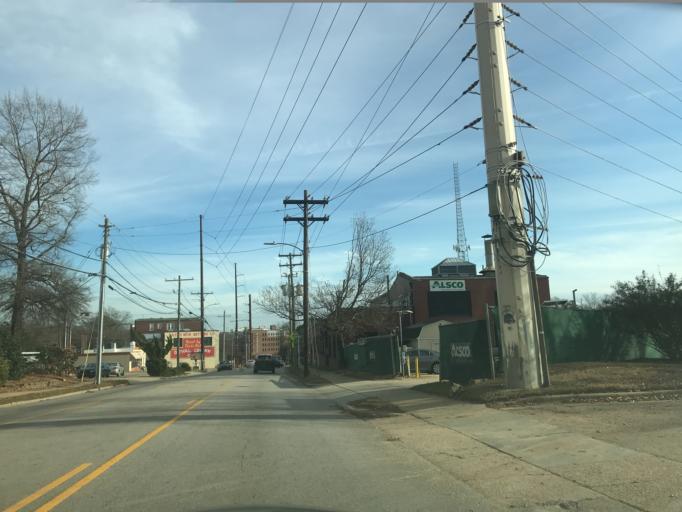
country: US
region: North Carolina
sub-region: Wake County
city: West Raleigh
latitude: 35.7916
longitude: -78.6812
